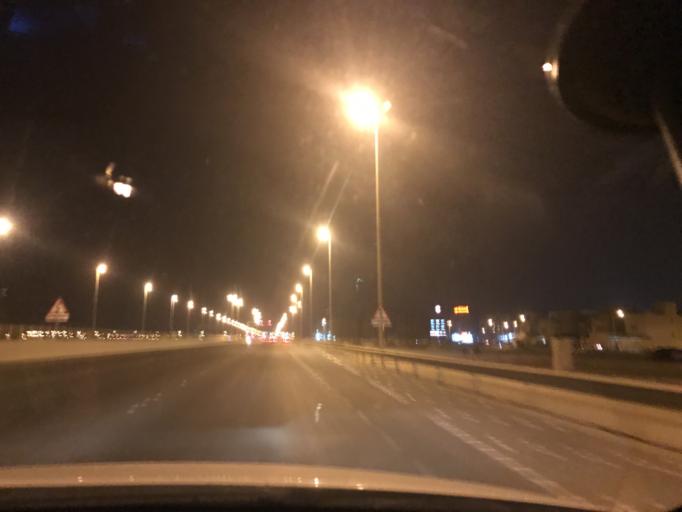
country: BH
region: Muharraq
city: Al Hadd
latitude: 26.2849
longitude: 50.6424
